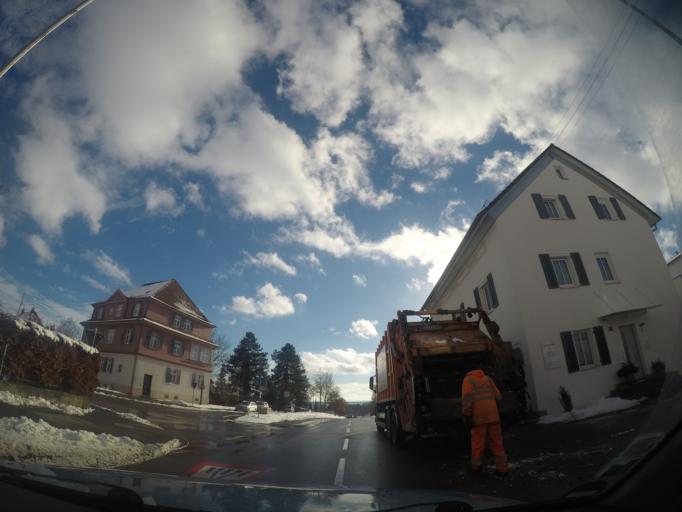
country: DE
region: Baden-Wuerttemberg
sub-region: Tuebingen Region
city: Ehingen
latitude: 48.2787
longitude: 9.7238
